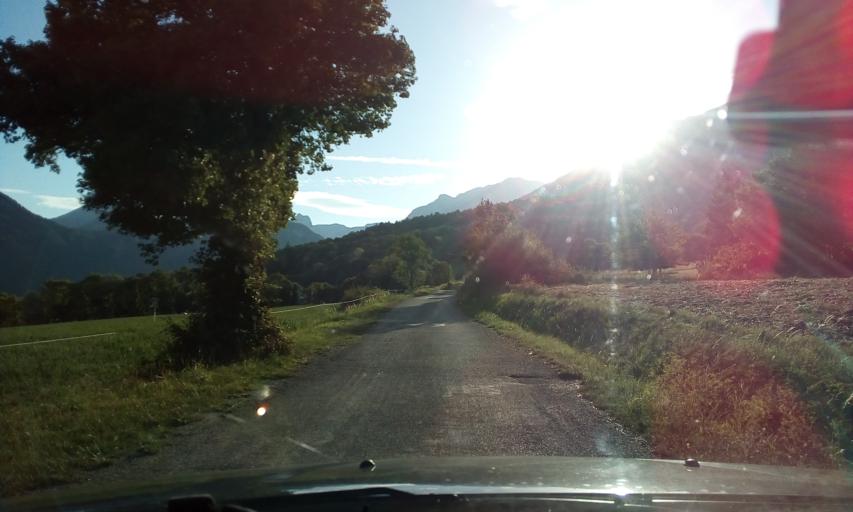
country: FR
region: Rhone-Alpes
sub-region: Departement de l'Isere
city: La Motte-Saint-Martin
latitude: 44.8779
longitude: 5.6157
